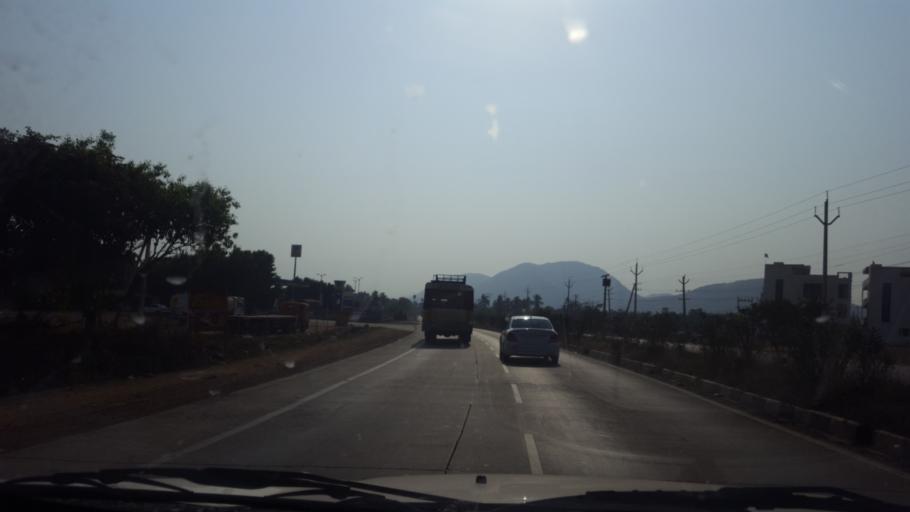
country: IN
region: Andhra Pradesh
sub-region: Vishakhapatnam
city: Anakapalle
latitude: 17.6461
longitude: 82.9091
